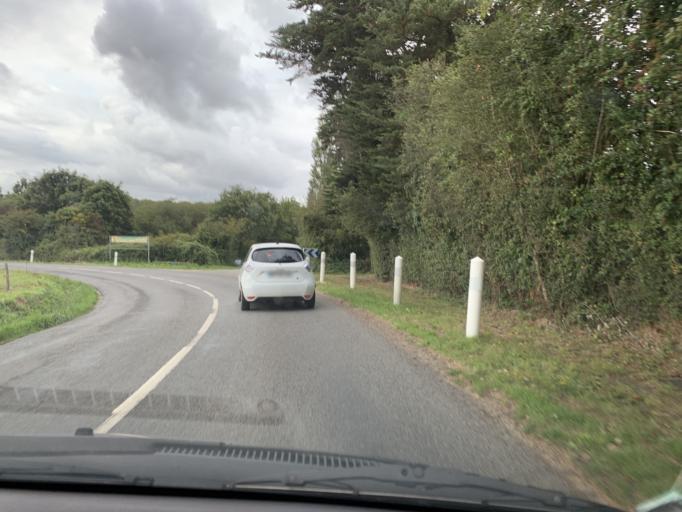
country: FR
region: Pays de la Loire
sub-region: Departement de la Loire-Atlantique
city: Asserac
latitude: 47.4342
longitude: -2.3979
